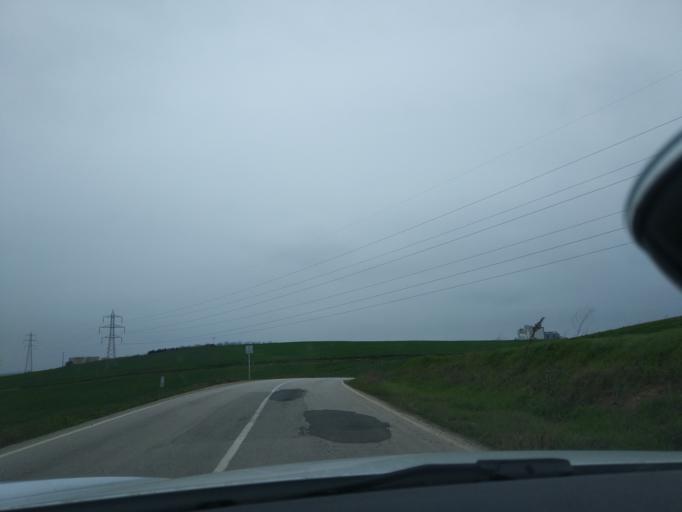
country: TR
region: Tekirdag
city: Marmara Ereglisi
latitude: 41.0286
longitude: 27.8461
